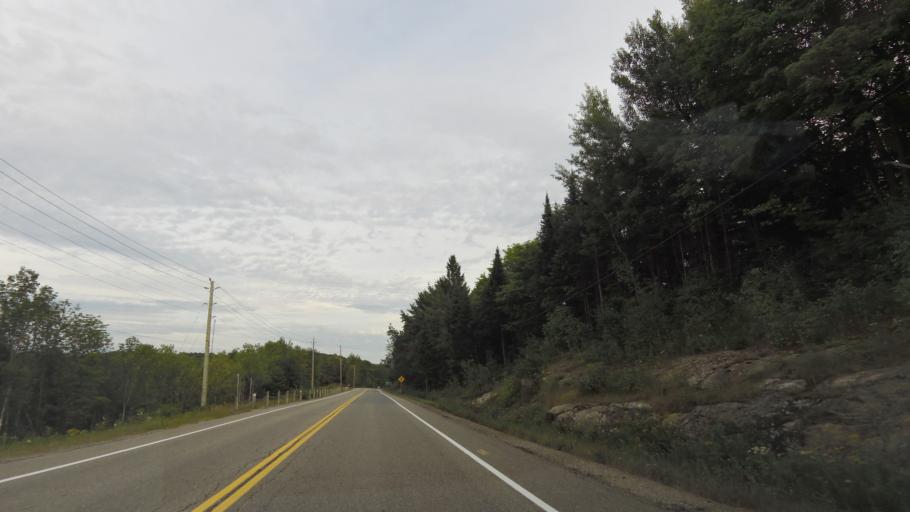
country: CA
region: Ontario
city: Bancroft
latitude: 45.0383
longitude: -78.4632
